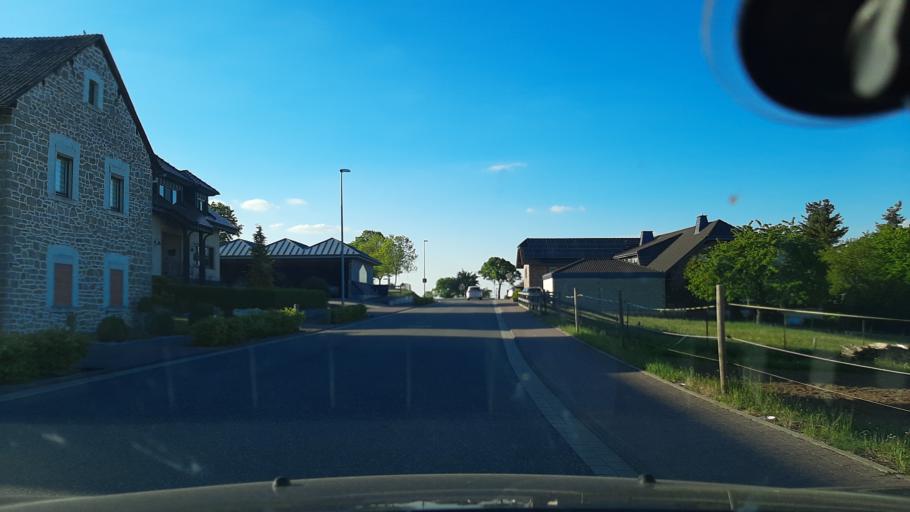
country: DE
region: Rheinland-Pfalz
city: Ohlenhard
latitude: 50.4748
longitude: 6.7136
